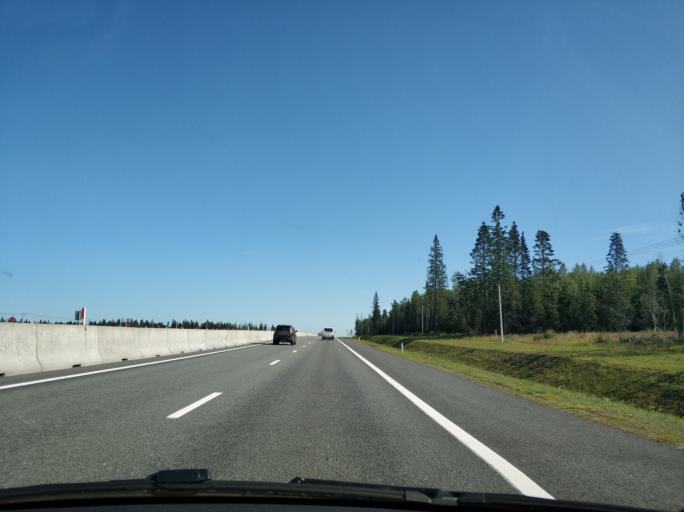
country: RU
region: Leningrad
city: Sosnovo
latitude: 60.4871
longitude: 30.1958
